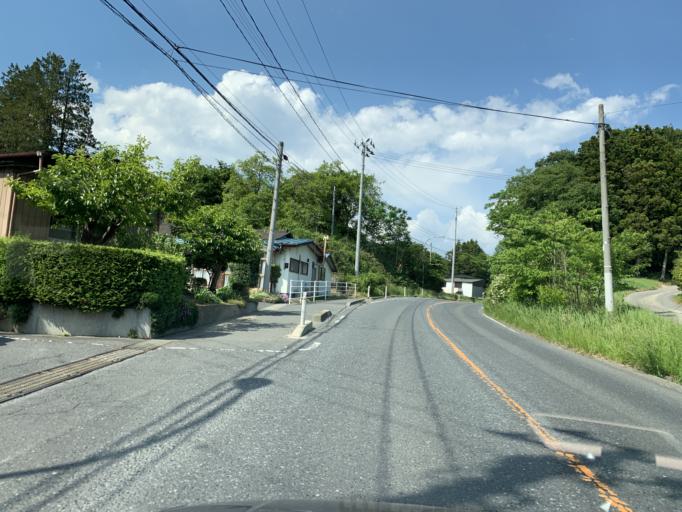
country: JP
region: Miyagi
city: Wakuya
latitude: 38.4903
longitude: 141.1086
